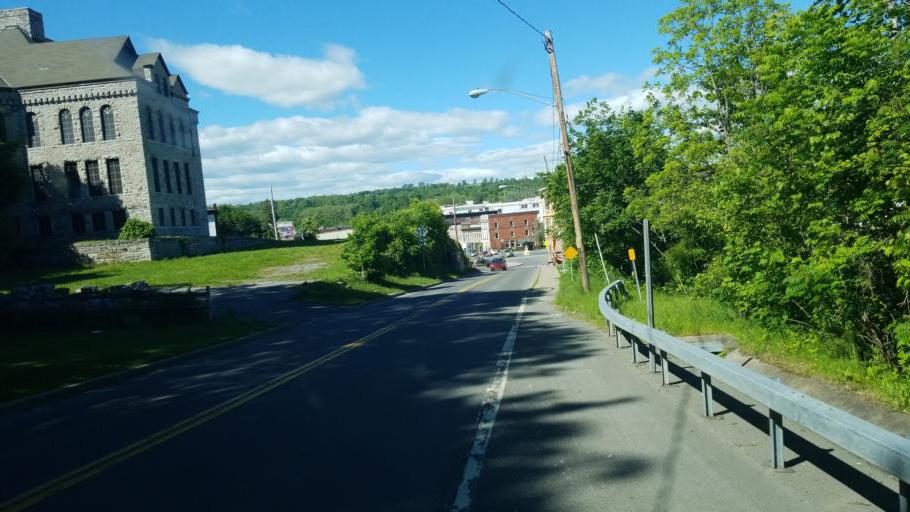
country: US
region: New York
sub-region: Montgomery County
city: Canajoharie
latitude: 42.9040
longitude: -74.5734
